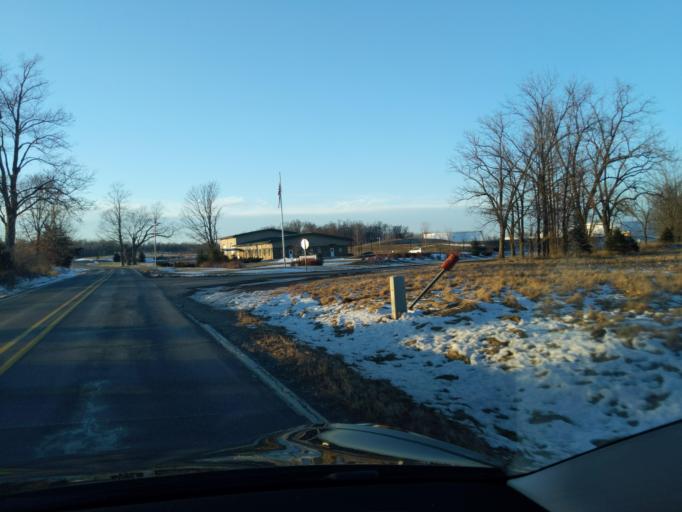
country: US
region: Michigan
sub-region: Ingham County
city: Stockbridge
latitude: 42.5016
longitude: -84.2347
